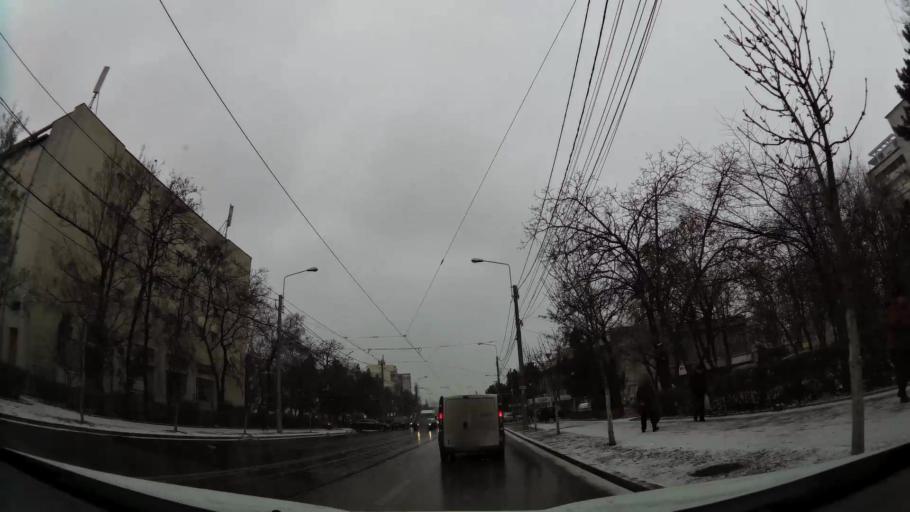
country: RO
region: Prahova
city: Ploiesti
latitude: 44.9542
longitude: 26.0024
